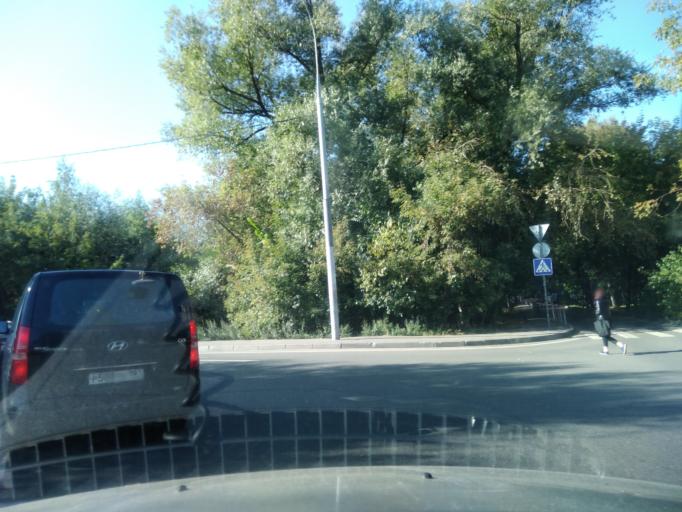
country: RU
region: Moscow
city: Strogino
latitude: 55.8515
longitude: 37.3873
